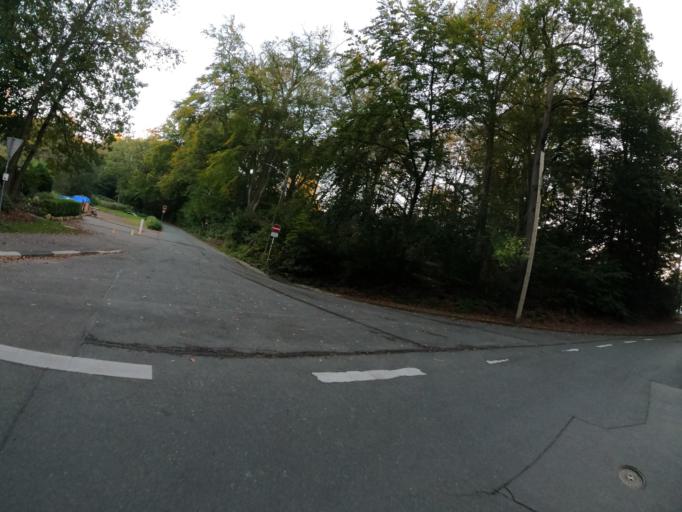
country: DE
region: North Rhine-Westphalia
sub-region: Regierungsbezirk Dusseldorf
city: Wuppertal
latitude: 51.2325
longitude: 7.1361
